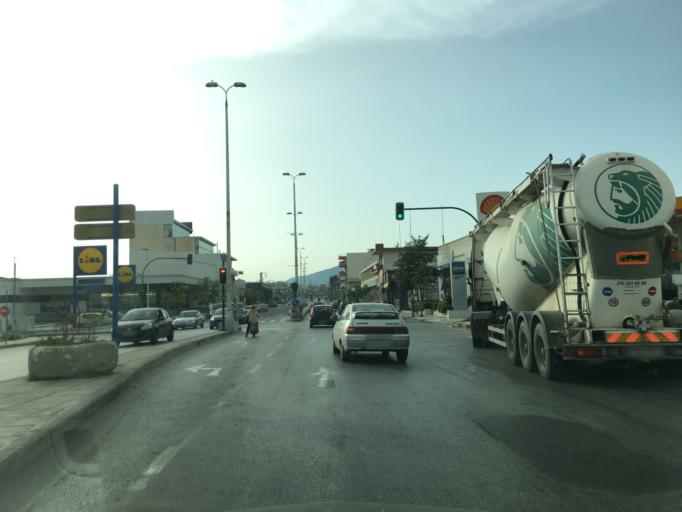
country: GR
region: Thessaly
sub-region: Nomos Magnisias
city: Nea Ionia
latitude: 39.3633
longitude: 22.9305
